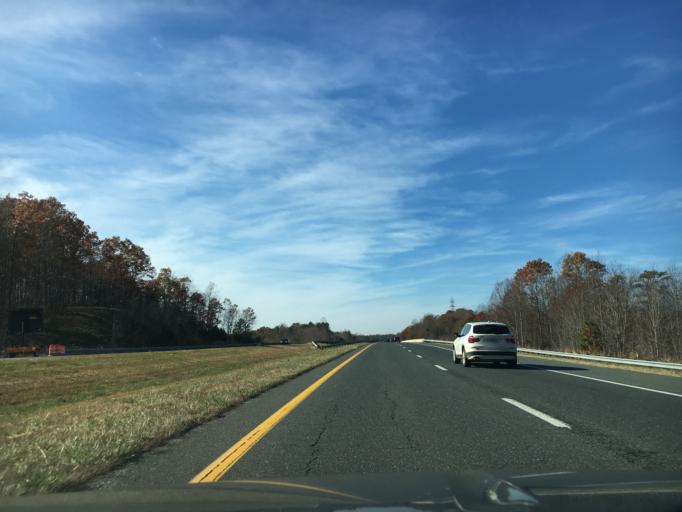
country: US
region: Virginia
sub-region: Amherst County
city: Madison Heights
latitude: 37.3853
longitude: -79.0870
